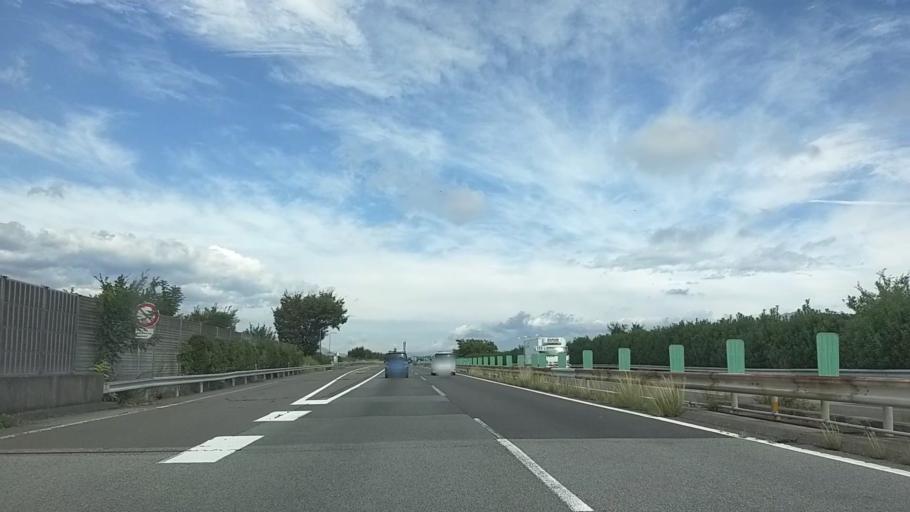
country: JP
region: Yamanashi
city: Kofu-shi
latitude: 35.6292
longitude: 138.5439
